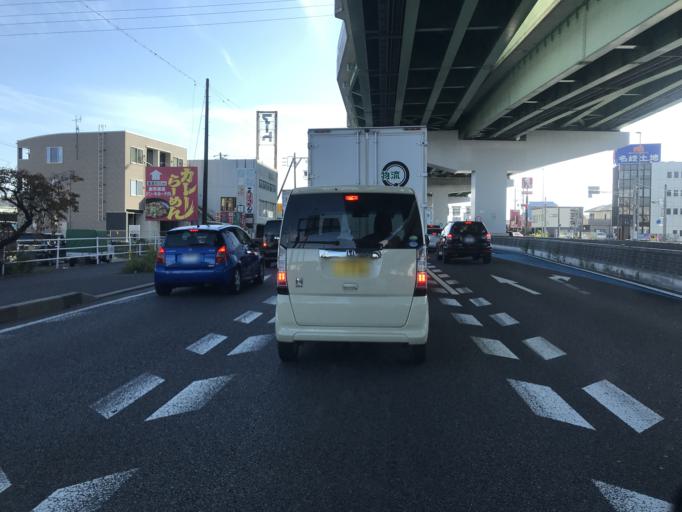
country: JP
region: Aichi
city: Iwakura
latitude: 35.2476
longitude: 136.8449
